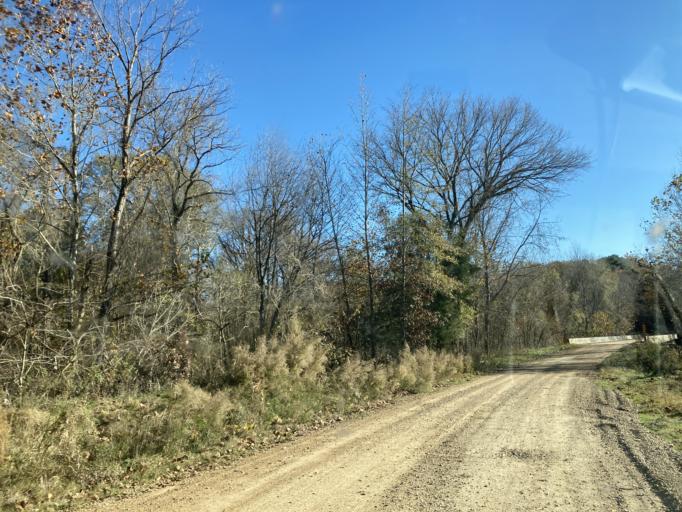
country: US
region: Mississippi
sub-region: Yazoo County
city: Yazoo City
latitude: 32.7062
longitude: -90.4711
